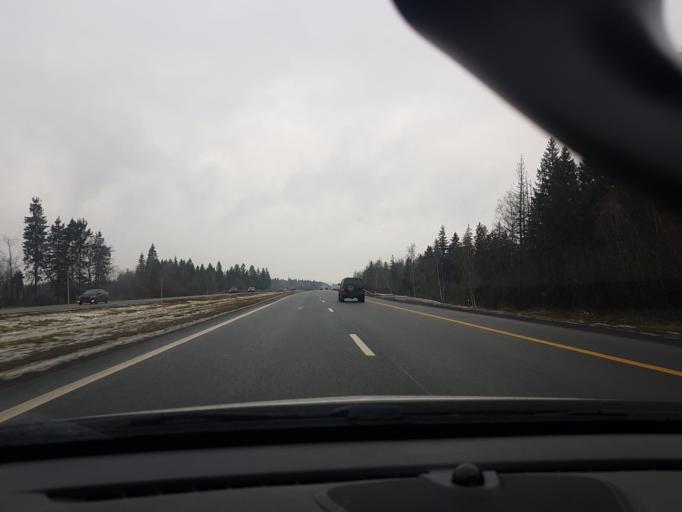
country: RU
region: Moskovskaya
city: Novopetrovskoye
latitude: 55.9815
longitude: 36.3794
